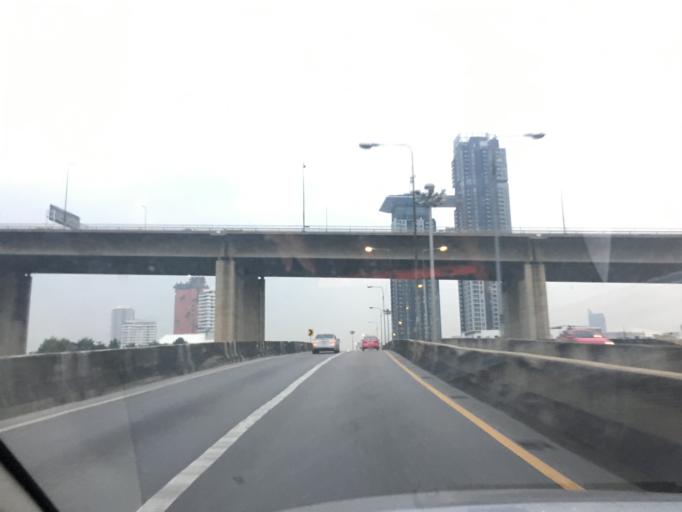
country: TH
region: Bangkok
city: Rat Burana
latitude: 13.6854
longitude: 100.5213
